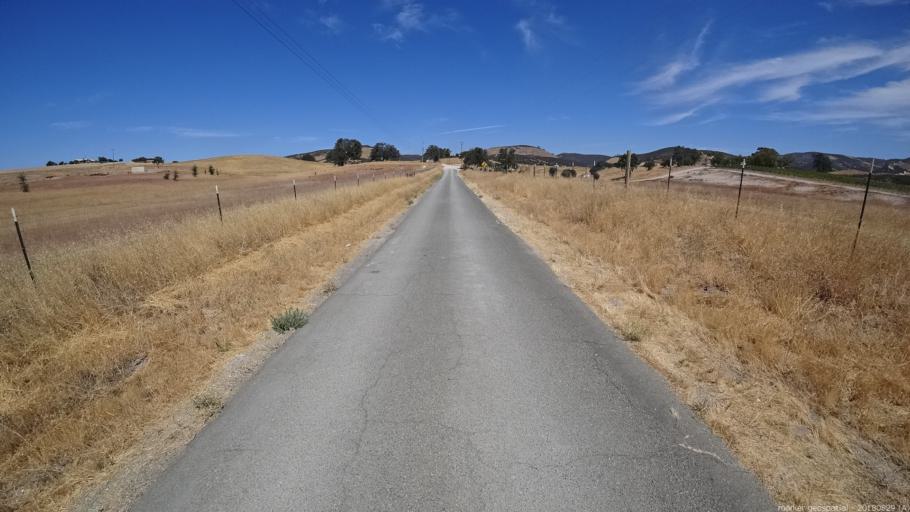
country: US
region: California
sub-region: Monterey County
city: King City
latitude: 35.9495
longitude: -121.0646
